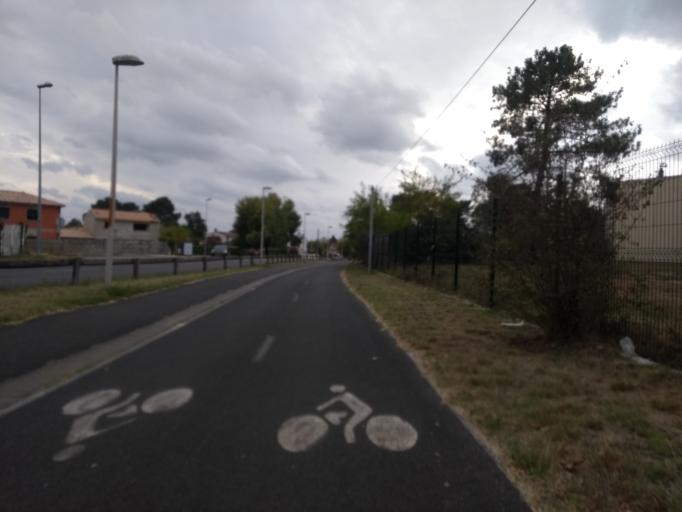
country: FR
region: Aquitaine
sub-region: Departement de la Gironde
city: Talence
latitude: 44.7838
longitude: -0.5930
